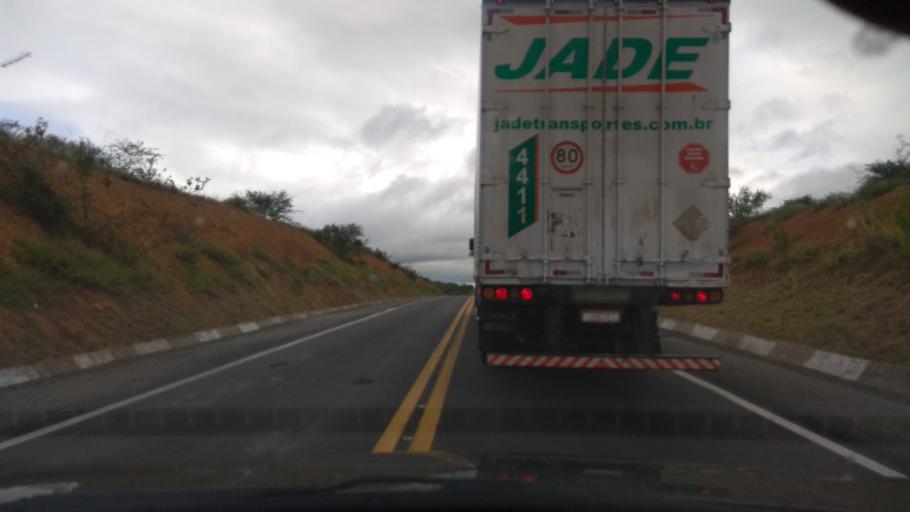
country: BR
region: Bahia
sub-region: Santa Ines
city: Santa Ines
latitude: -13.2780
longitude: -40.0158
